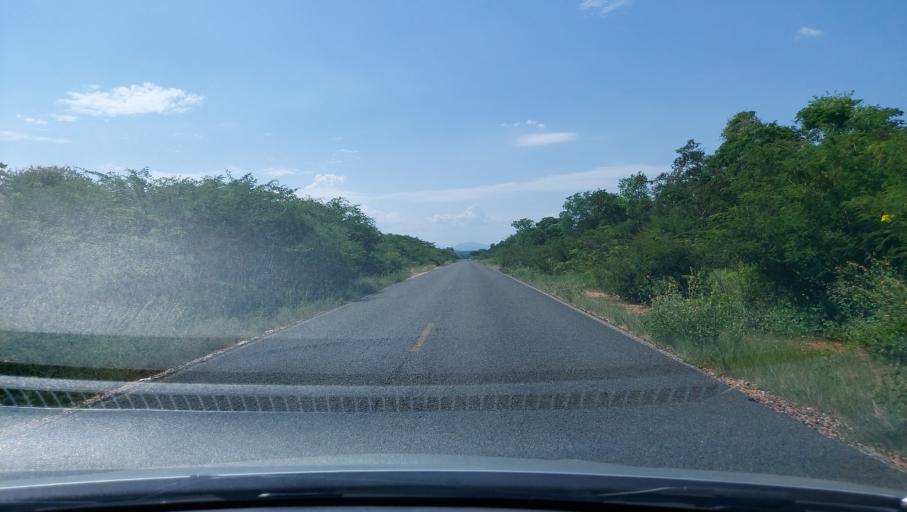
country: BR
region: Bahia
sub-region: Oliveira Dos Brejinhos
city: Beira Rio
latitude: -12.1809
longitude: -42.5418
